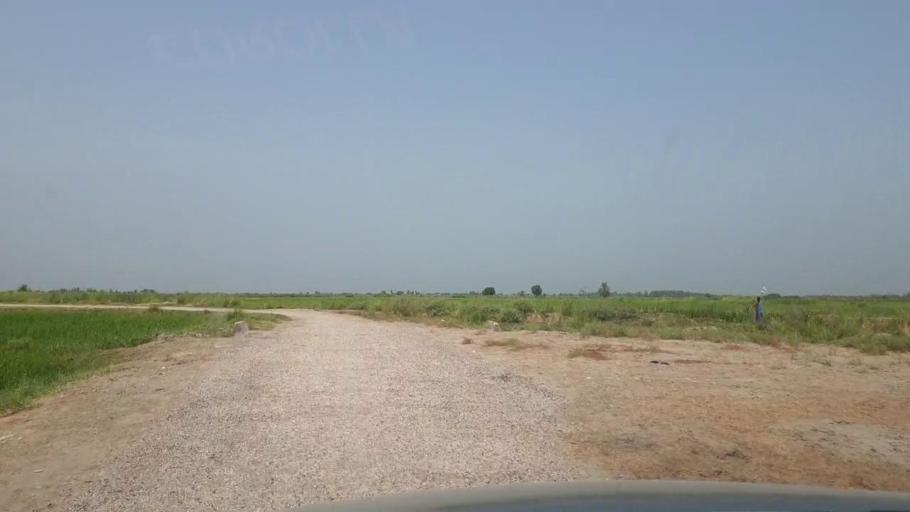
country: PK
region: Sindh
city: Madeji
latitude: 27.8146
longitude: 68.5139
